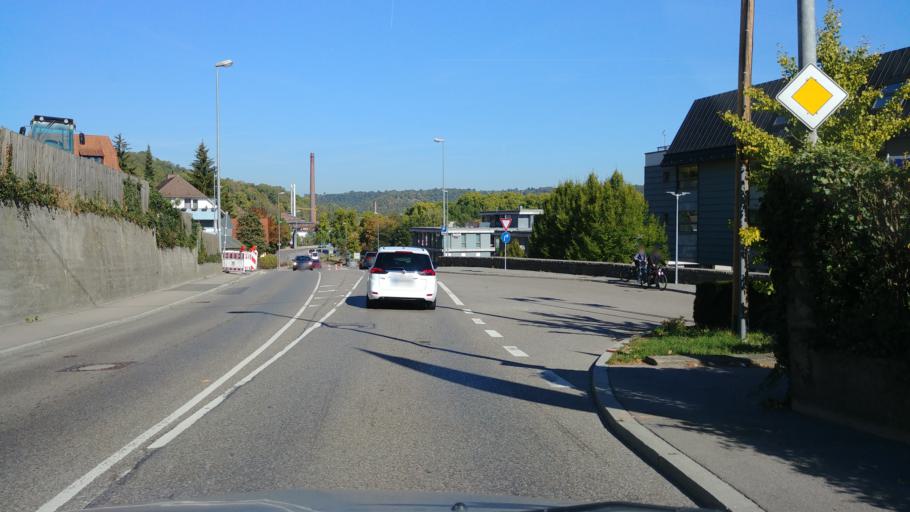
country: DE
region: Baden-Wuerttemberg
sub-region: Regierungsbezirk Stuttgart
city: Schwaebisch Hall
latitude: 49.1149
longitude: 9.7321
